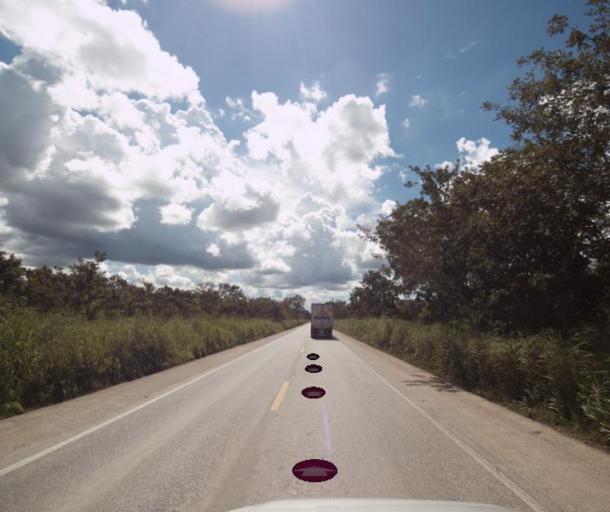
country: BR
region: Goias
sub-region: Porangatu
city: Porangatu
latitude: -13.5672
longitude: -49.0515
